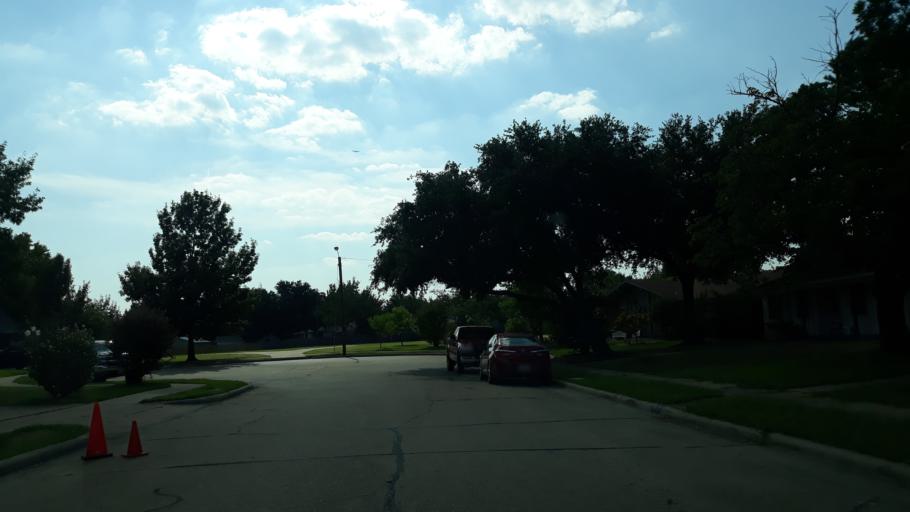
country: US
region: Texas
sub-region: Dallas County
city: Irving
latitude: 32.8501
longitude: -97.0020
